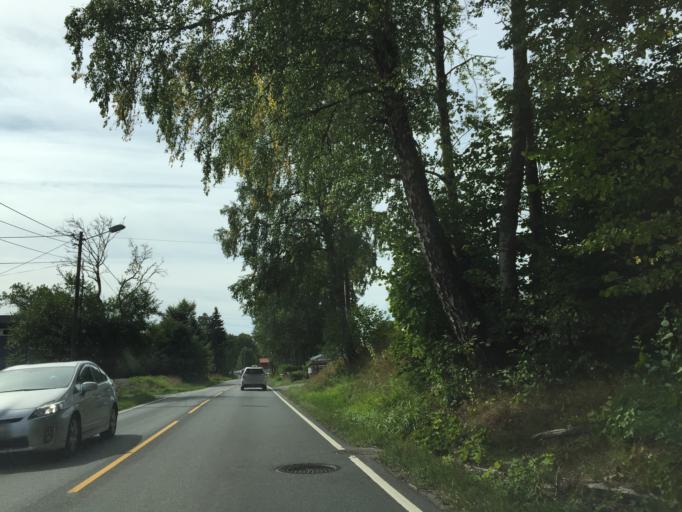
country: NO
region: Ostfold
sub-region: Moss
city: Moss
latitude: 59.4848
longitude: 10.6973
